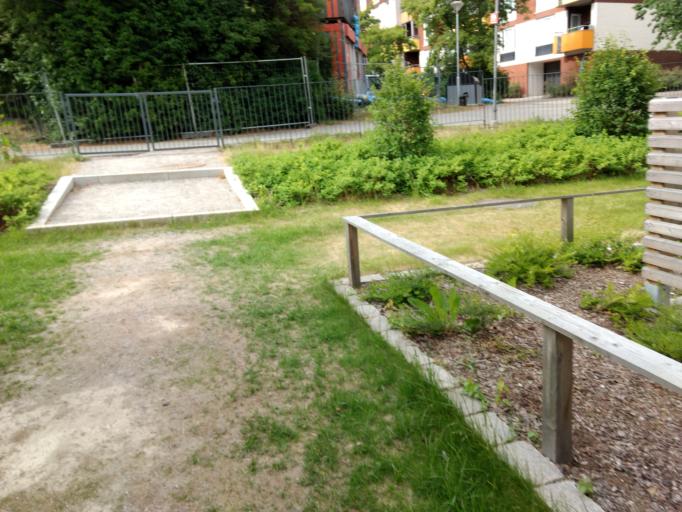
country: SE
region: Stockholm
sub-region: Upplands Vasby Kommun
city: Upplands Vaesby
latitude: 59.5270
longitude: 17.9135
